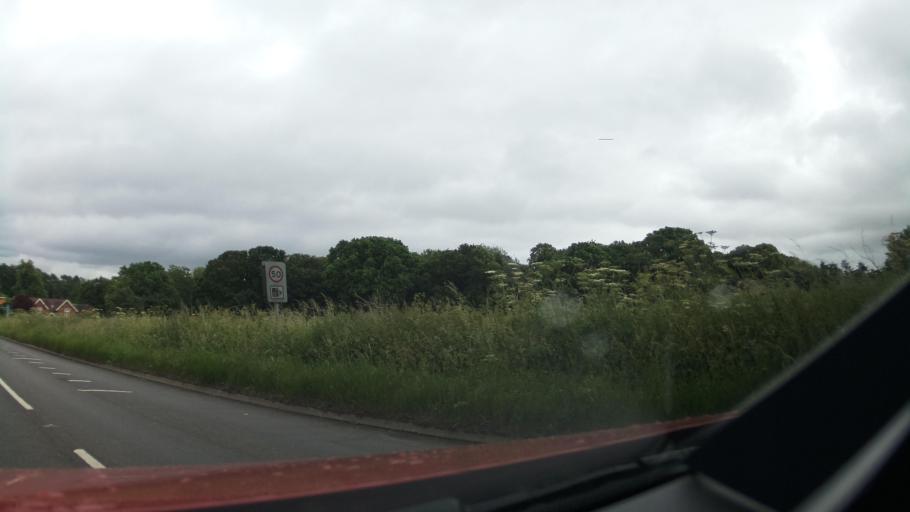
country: GB
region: England
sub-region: Staffordshire
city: Burton upon Trent
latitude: 52.8409
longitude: -1.6689
